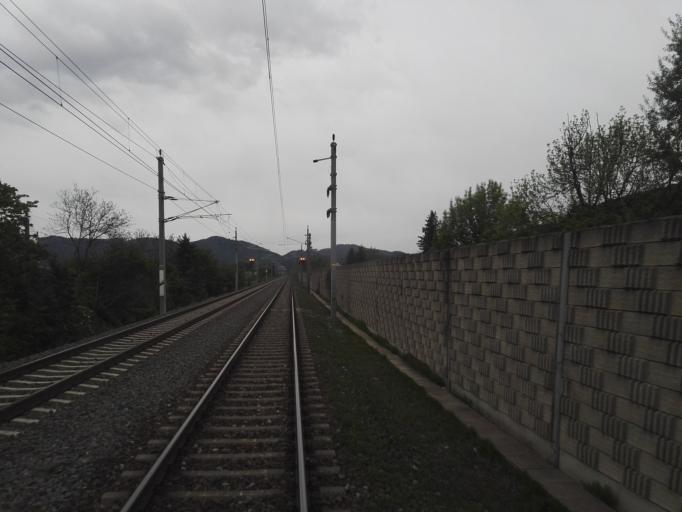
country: AT
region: Styria
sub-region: Politischer Bezirk Graz-Umgebung
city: Gratkorn
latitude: 47.1452
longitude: 15.3247
